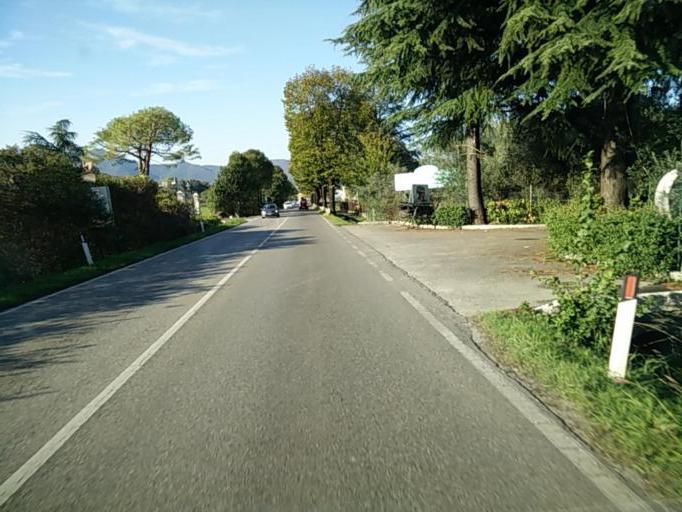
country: IT
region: Lombardy
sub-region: Provincia di Brescia
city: Raffa
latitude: 45.5789
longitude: 10.5237
